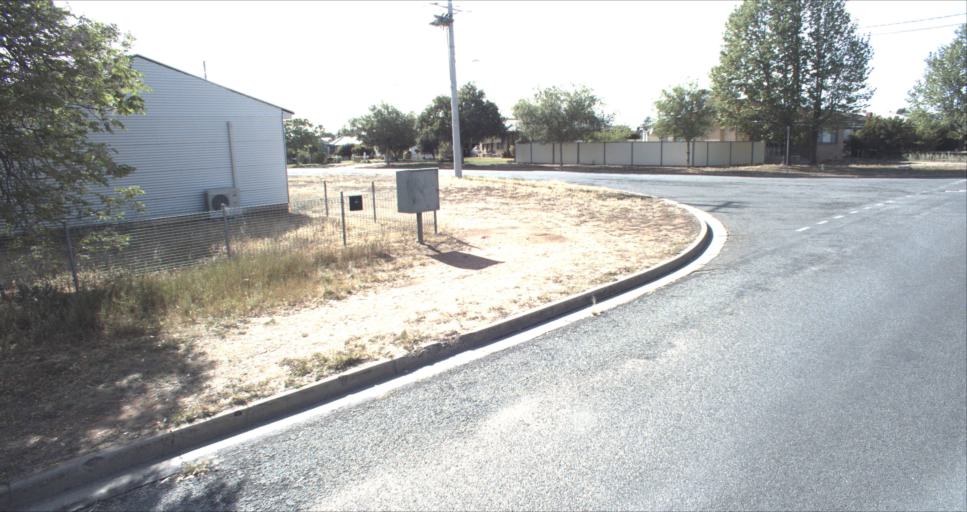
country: AU
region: New South Wales
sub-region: Leeton
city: Leeton
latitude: -34.5578
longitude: 146.4093
